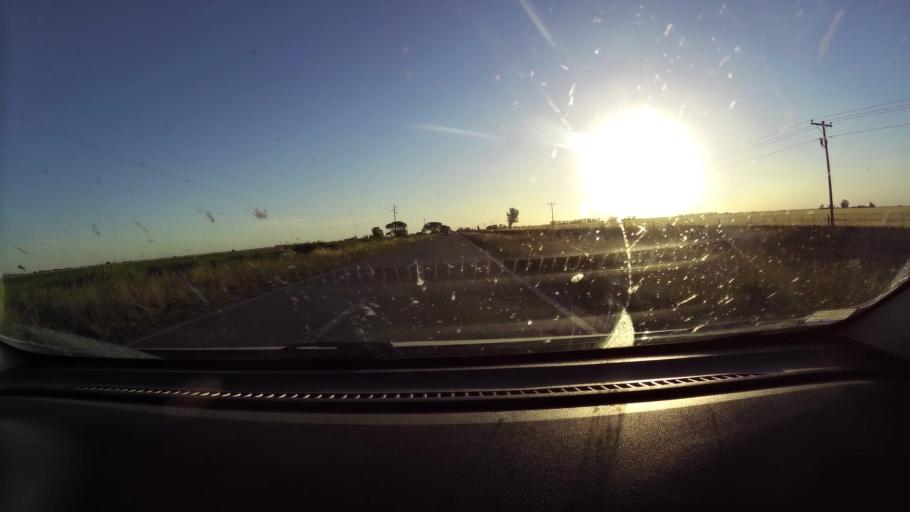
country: AR
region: Cordoba
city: Pozo del Molle
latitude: -32.0559
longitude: -62.9709
